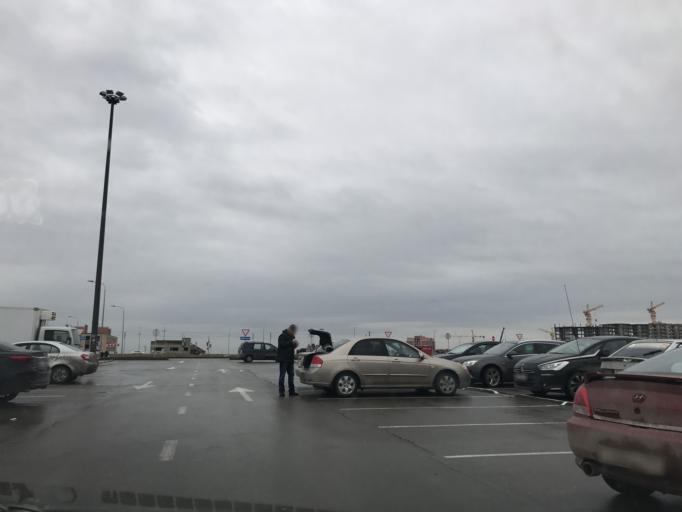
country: RU
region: Rostov
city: Severnyy
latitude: 47.3088
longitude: 39.7239
